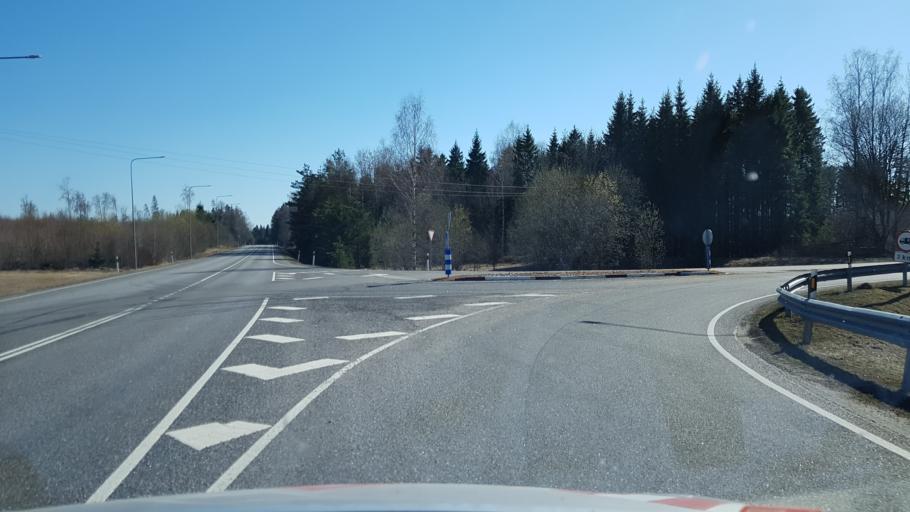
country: EE
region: Laeaene-Virumaa
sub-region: Vaeike-Maarja vald
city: Vaike-Maarja
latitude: 59.0995
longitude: 26.2275
